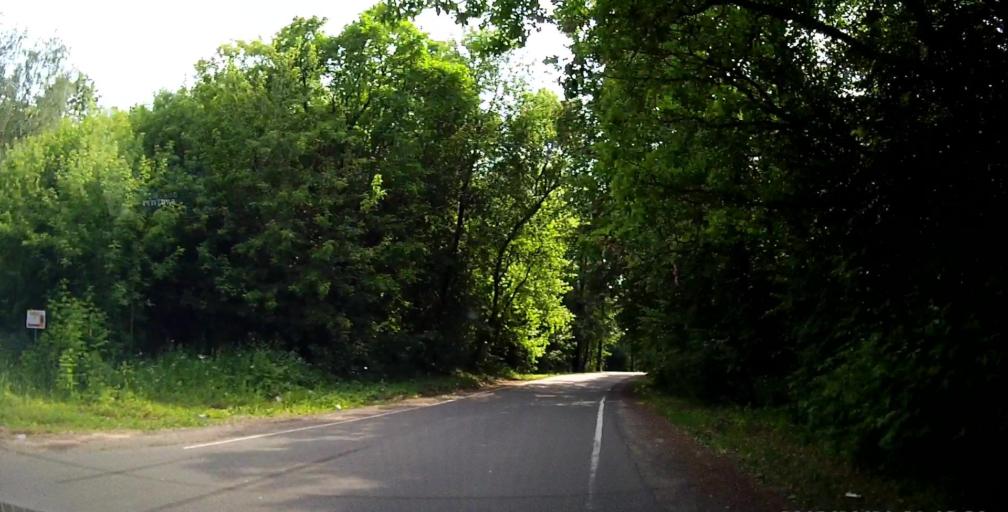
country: RU
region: Moskovskaya
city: Dubrovitsy
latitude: 55.4099
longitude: 37.4824
